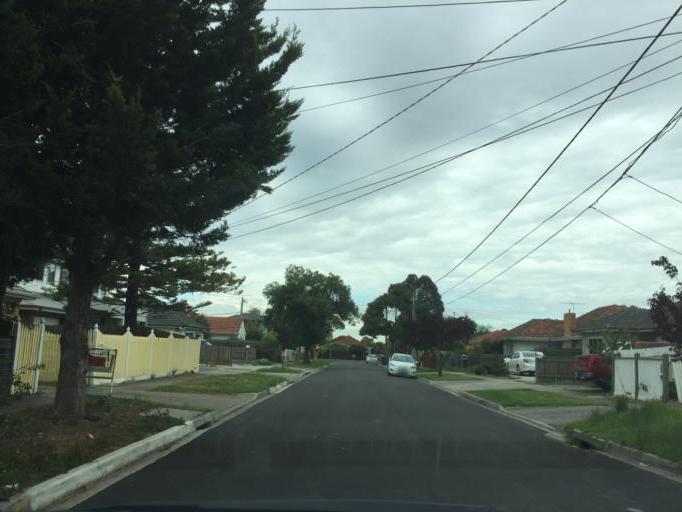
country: AU
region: Victoria
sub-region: Brimbank
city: Albion
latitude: -37.7786
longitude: 144.8383
